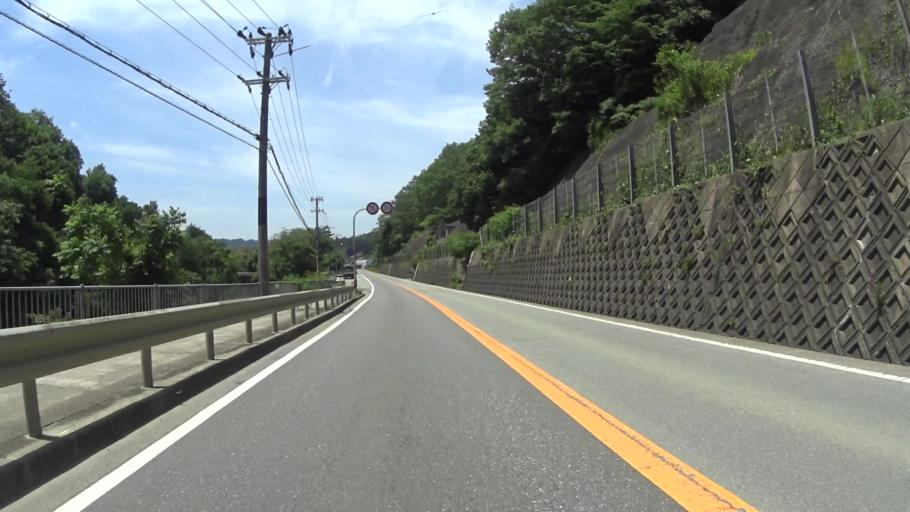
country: JP
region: Kyoto
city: Ayabe
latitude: 35.1785
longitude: 135.3930
